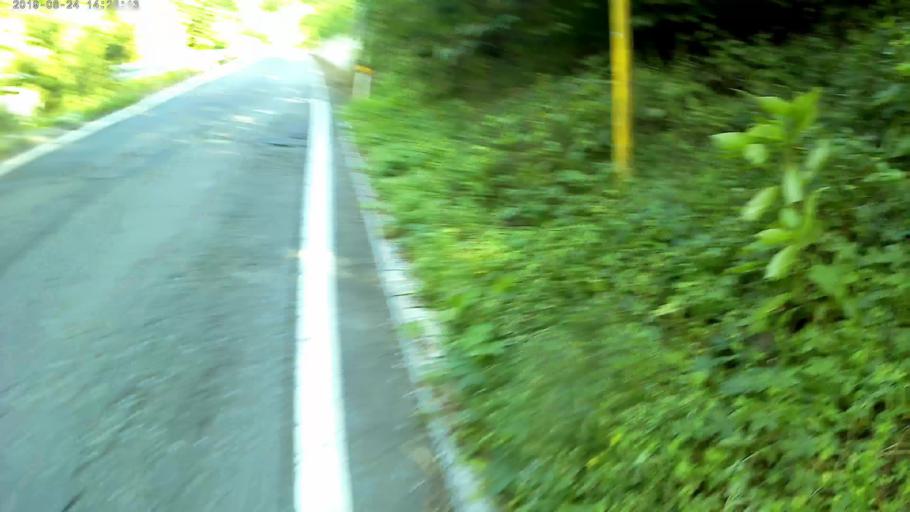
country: JP
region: Nagano
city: Komoro
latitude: 36.2698
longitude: 138.4293
